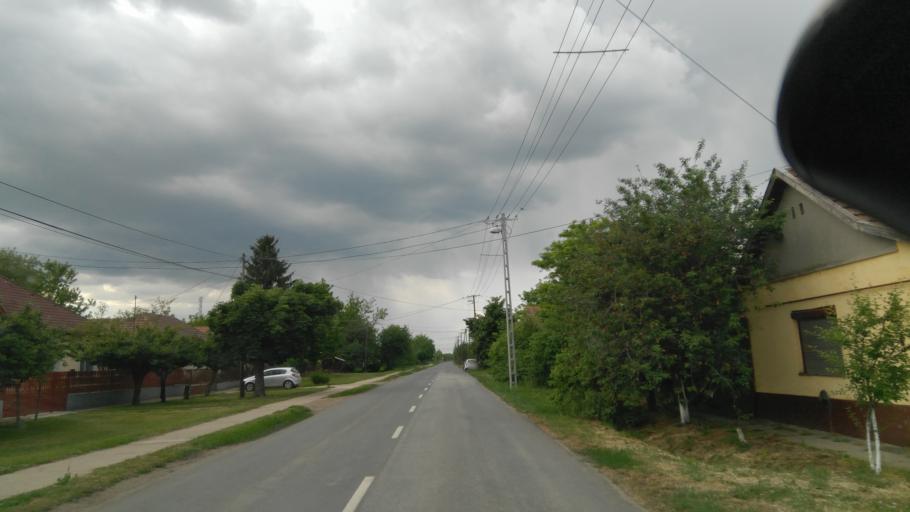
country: HU
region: Bekes
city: Dombegyhaz
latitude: 46.3475
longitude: 21.1229
